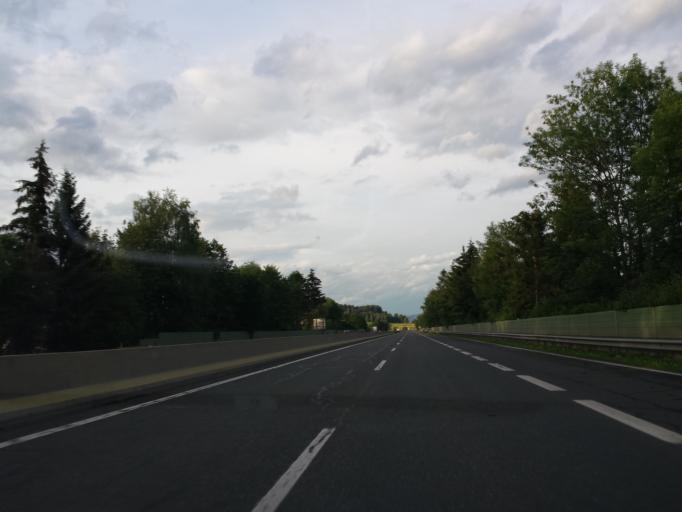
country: AT
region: Styria
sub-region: Politischer Bezirk Murtal
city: Knittelfeld
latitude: 47.2182
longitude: 14.8036
